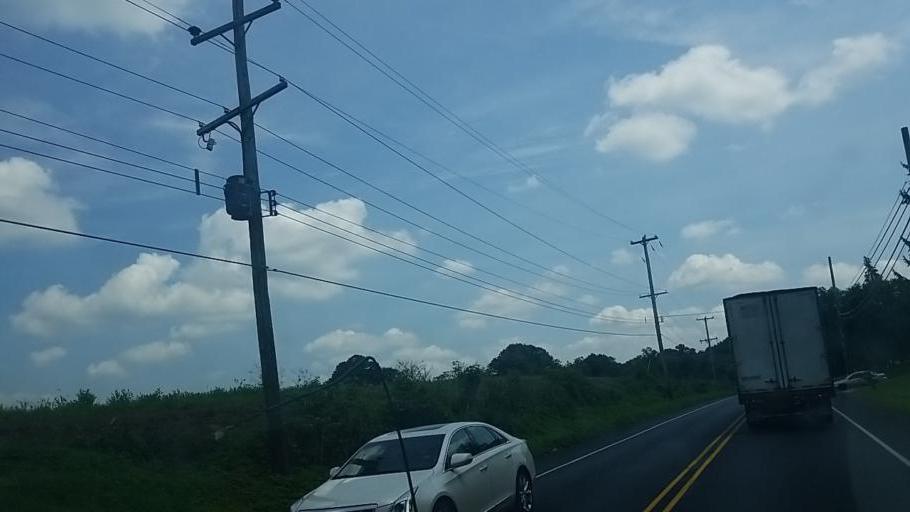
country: US
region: Pennsylvania
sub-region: Chester County
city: Toughkenamon
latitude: 39.8147
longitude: -75.7643
